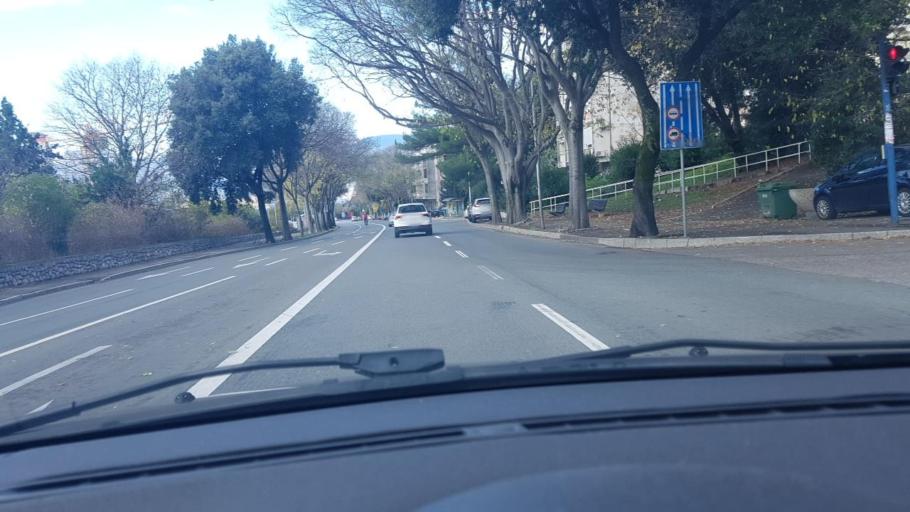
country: HR
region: Primorsko-Goranska
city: Rijeka
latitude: 45.3387
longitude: 14.4027
